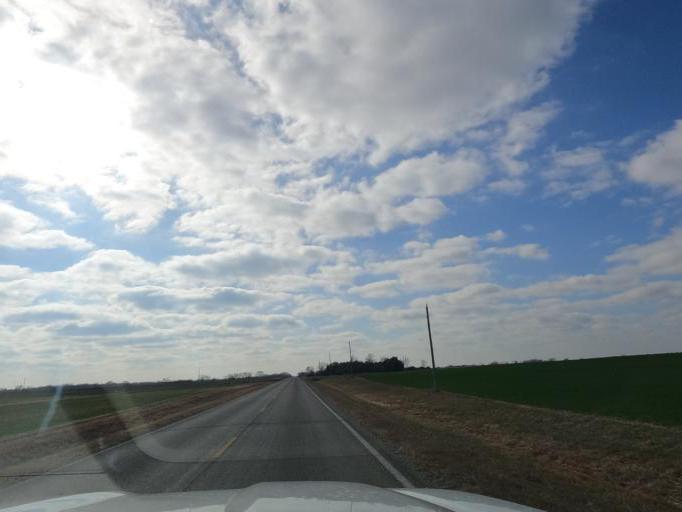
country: US
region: Kansas
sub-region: McPherson County
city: Inman
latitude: 38.2320
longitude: -97.8642
